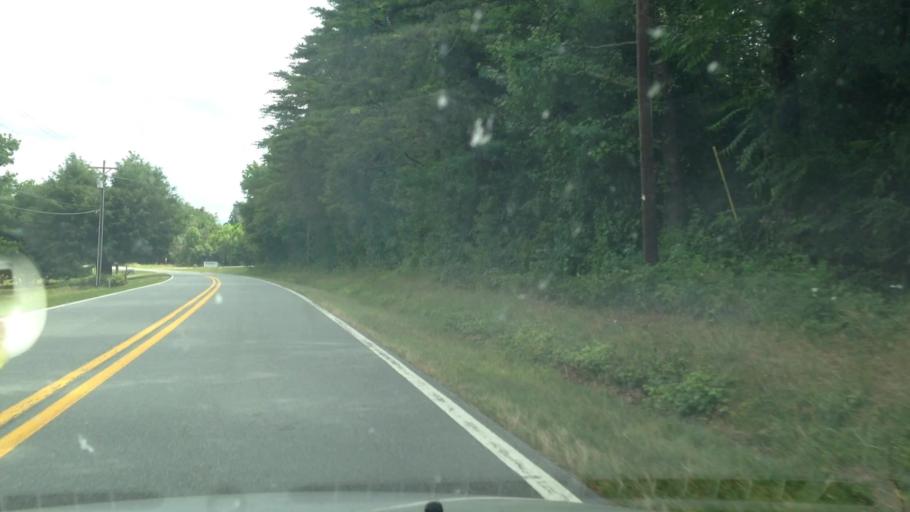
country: US
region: North Carolina
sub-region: Rockingham County
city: Reidsville
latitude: 36.4263
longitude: -79.5830
